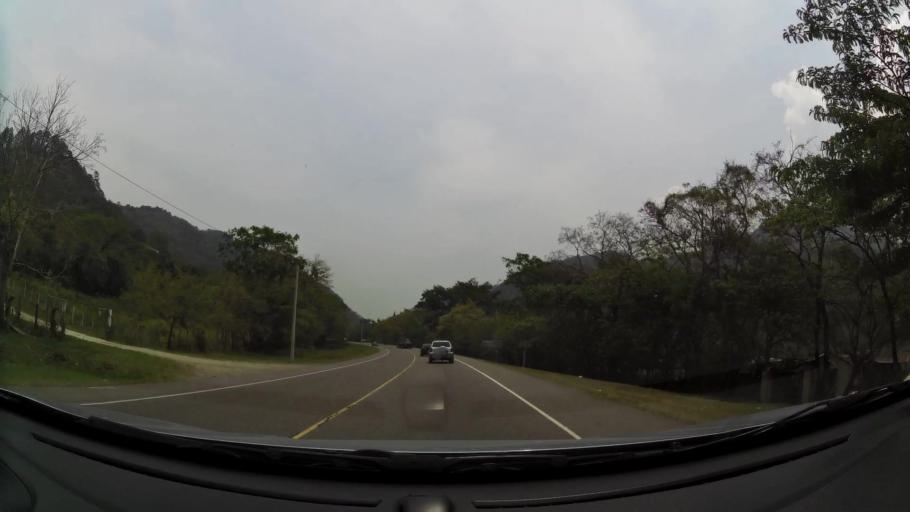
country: HN
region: Comayagua
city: Taulabe
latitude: 14.7200
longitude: -87.9648
